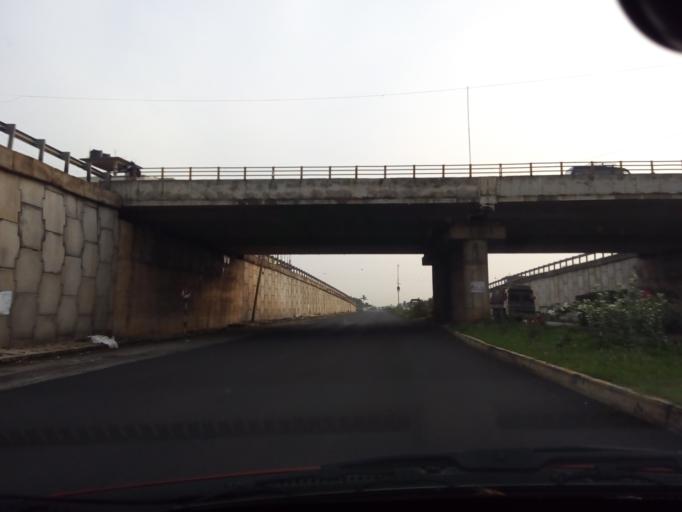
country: IN
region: Karnataka
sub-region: Chikkaballapur
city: Gudibanda
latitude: 13.5883
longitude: 77.7835
